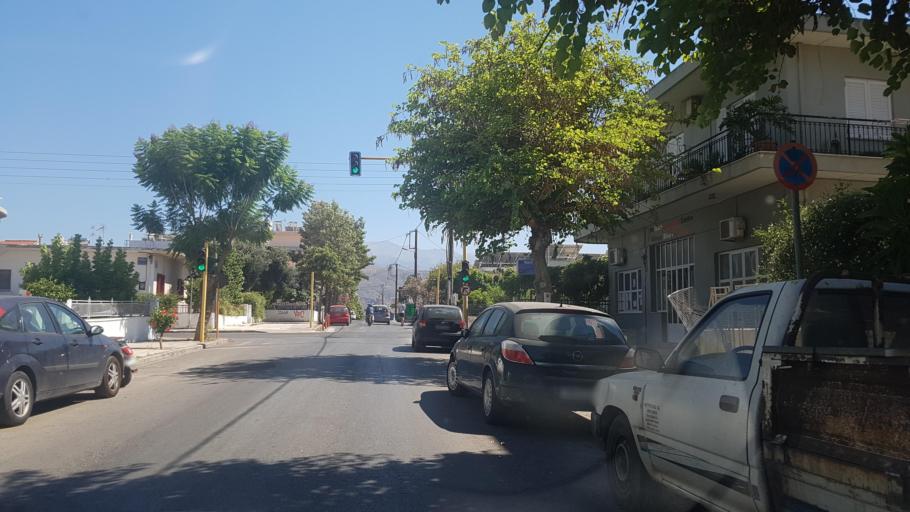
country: GR
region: Crete
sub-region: Nomos Chanias
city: Chania
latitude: 35.5082
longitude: 24.0176
